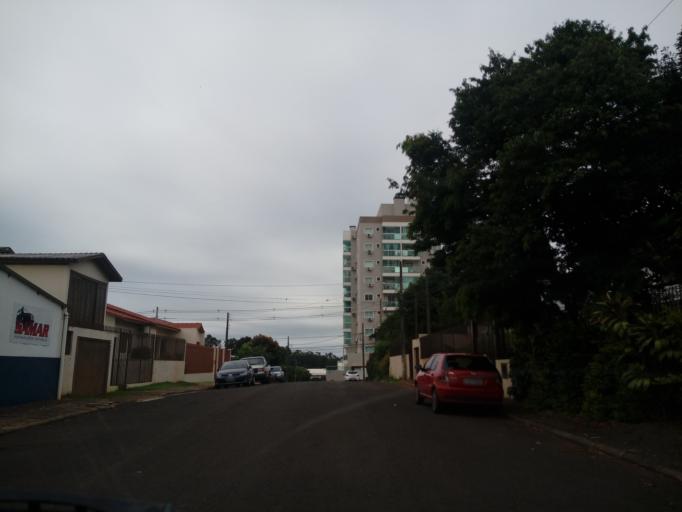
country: BR
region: Santa Catarina
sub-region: Chapeco
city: Chapeco
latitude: -27.0951
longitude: -52.6245
